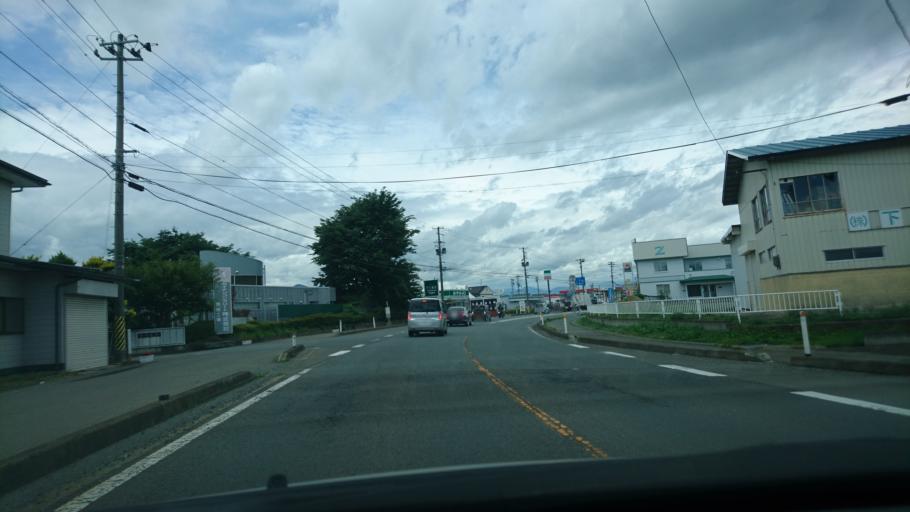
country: JP
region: Iwate
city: Morioka-shi
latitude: 39.6161
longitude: 141.1919
